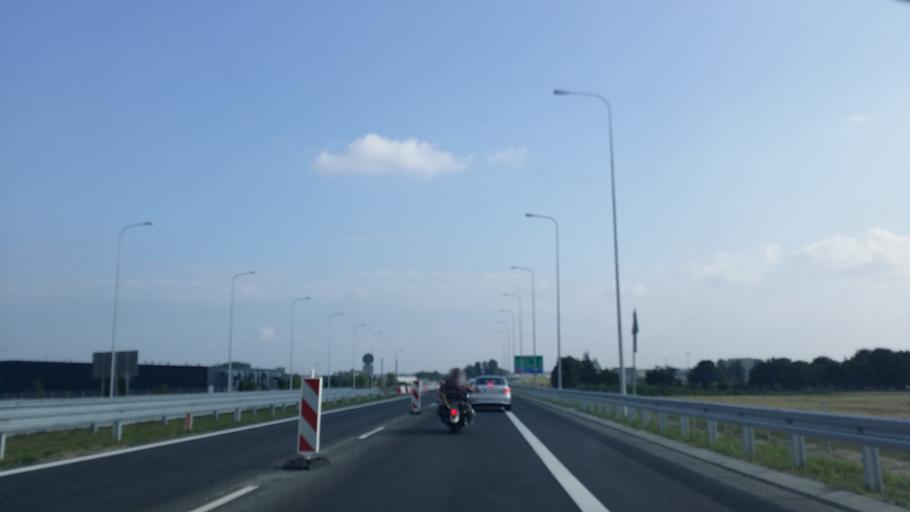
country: PL
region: Lubusz
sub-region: Powiat miedzyrzecki
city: Miedzyrzecz
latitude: 52.4593
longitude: 15.5640
